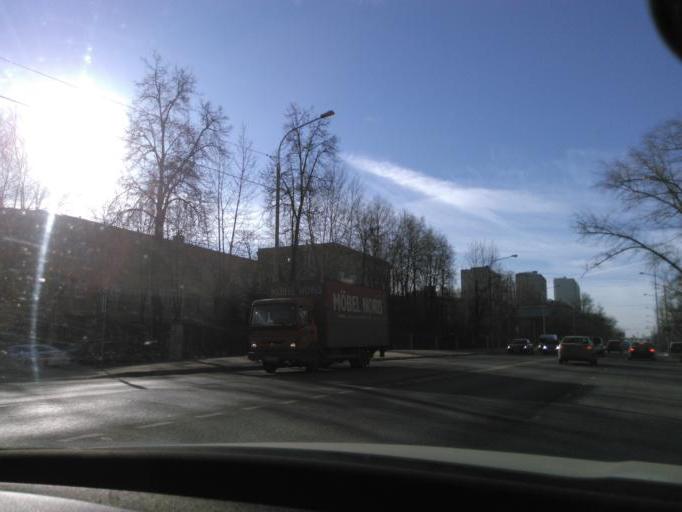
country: RU
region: Moscow
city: Zapadnoye Degunino
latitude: 55.8467
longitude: 37.5213
